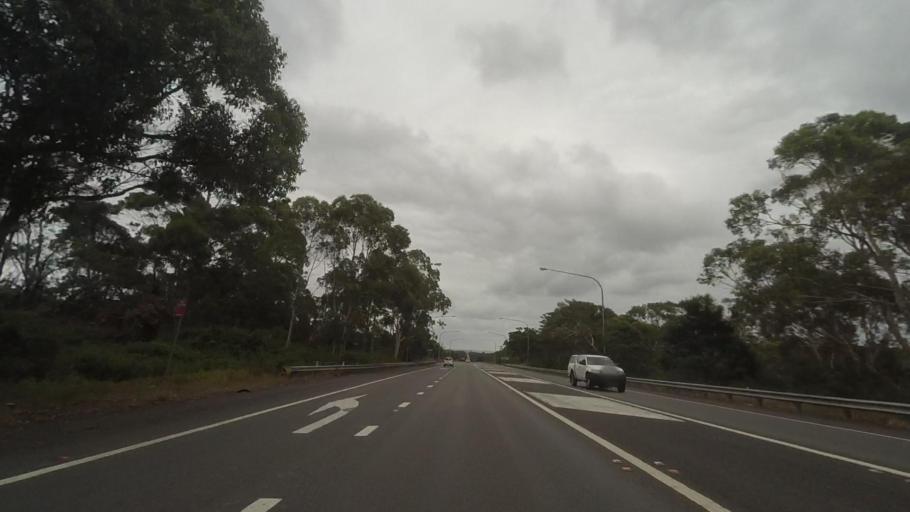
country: AU
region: New South Wales
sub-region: Wyong Shire
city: Charmhaven
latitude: -33.2054
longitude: 151.5002
